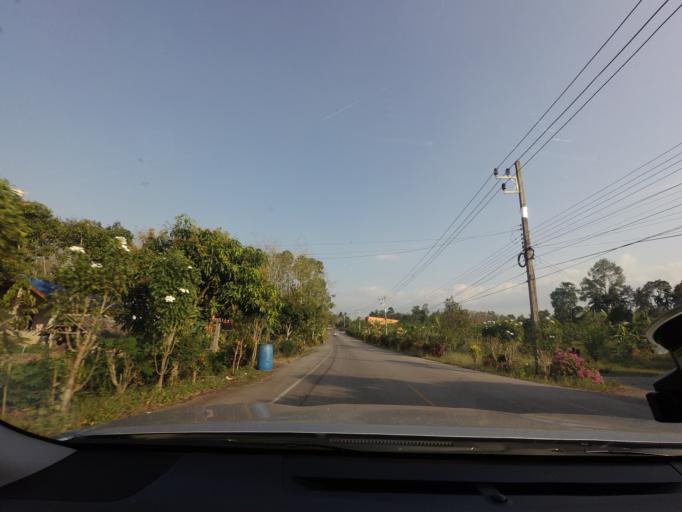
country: TH
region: Surat Thani
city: Phrasaeng
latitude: 8.5610
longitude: 99.2921
